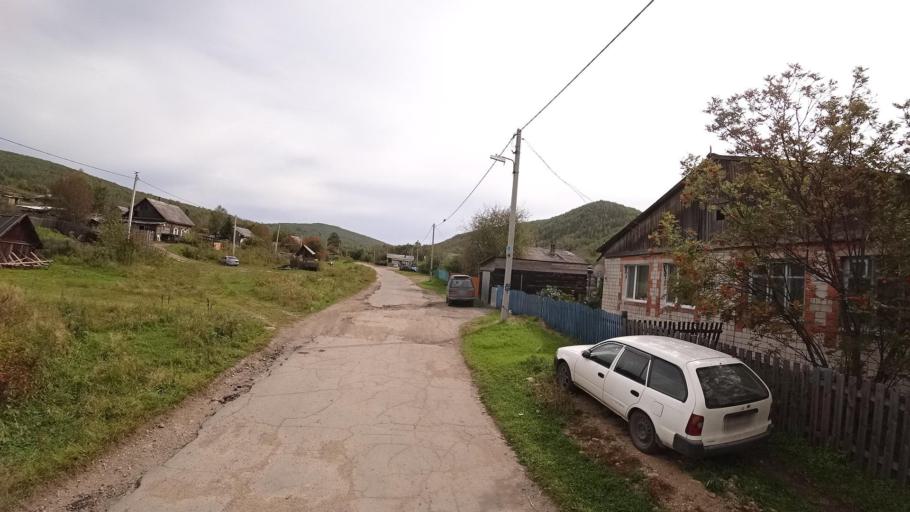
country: RU
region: Jewish Autonomous Oblast
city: Khingansk
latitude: 49.1229
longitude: 131.2047
